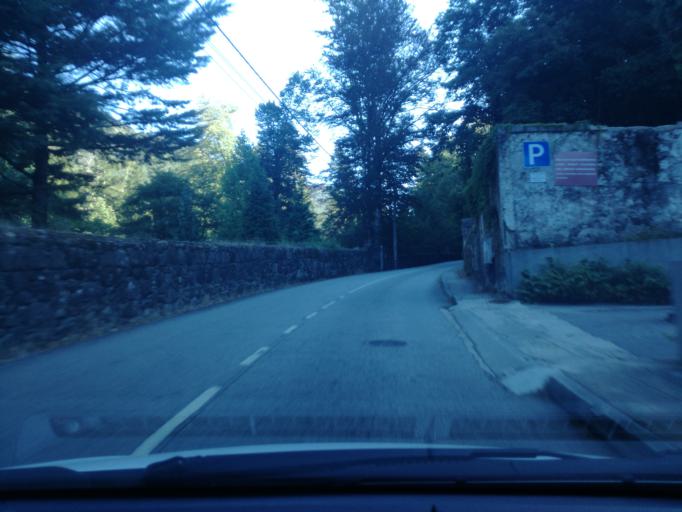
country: PT
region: Braga
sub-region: Vieira do Minho
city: Real
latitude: 41.7317
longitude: -8.1613
